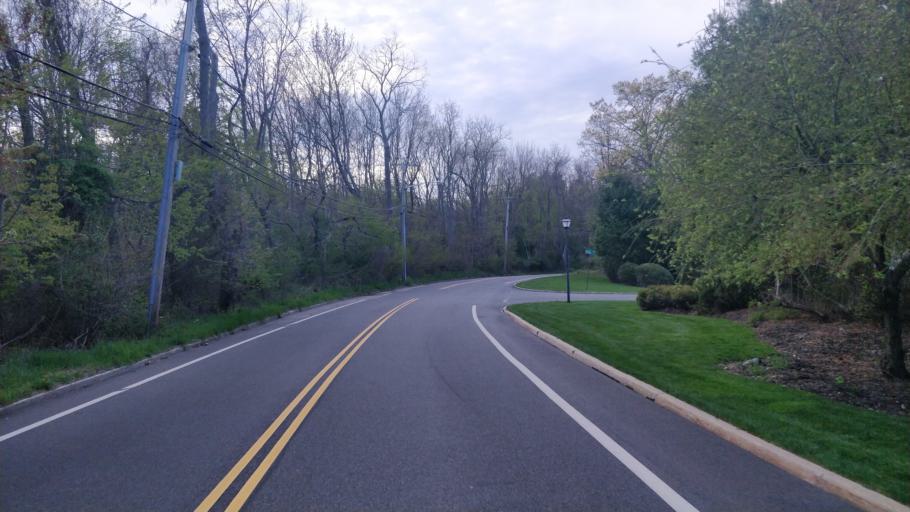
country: US
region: New York
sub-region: Suffolk County
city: Nissequogue
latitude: 40.8882
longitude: -73.2162
